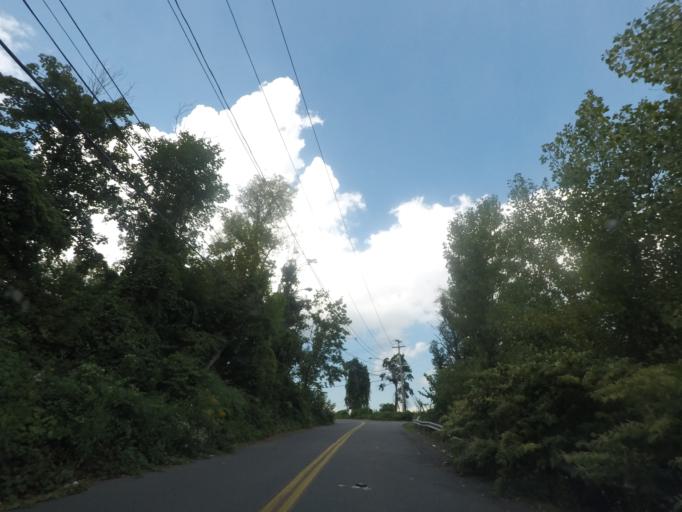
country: US
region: New York
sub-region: Rensselaer County
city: Troy
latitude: 42.7053
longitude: -73.6882
